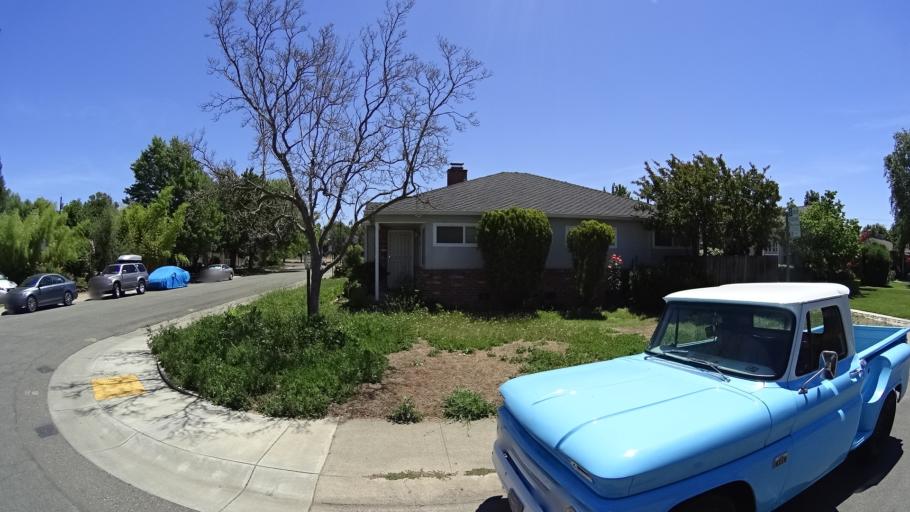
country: US
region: California
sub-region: Sacramento County
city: Sacramento
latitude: 38.5716
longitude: -121.4351
